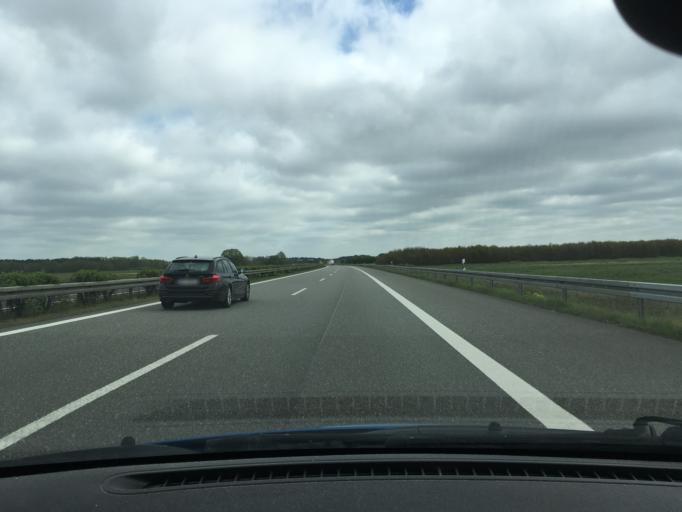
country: DE
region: Mecklenburg-Vorpommern
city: Sulstorf
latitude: 53.4734
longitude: 11.3072
